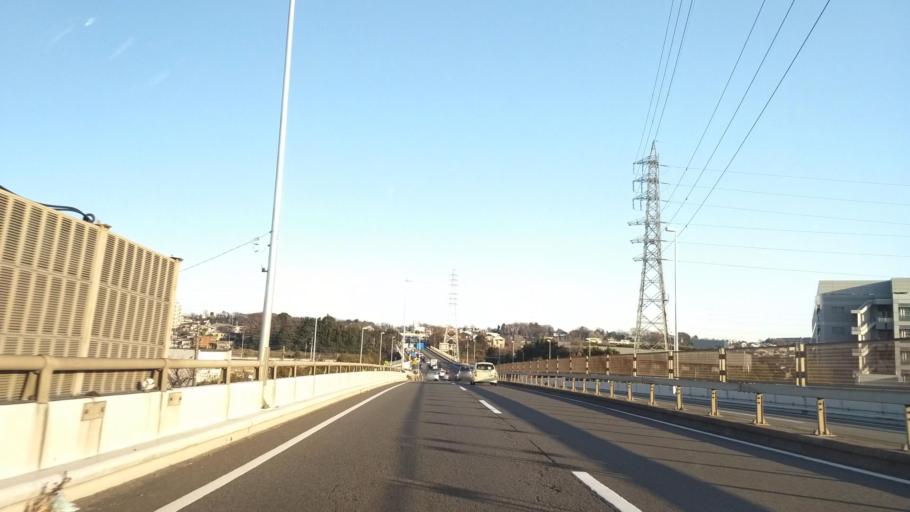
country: JP
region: Kanagawa
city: Zama
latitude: 35.4640
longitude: 139.3895
